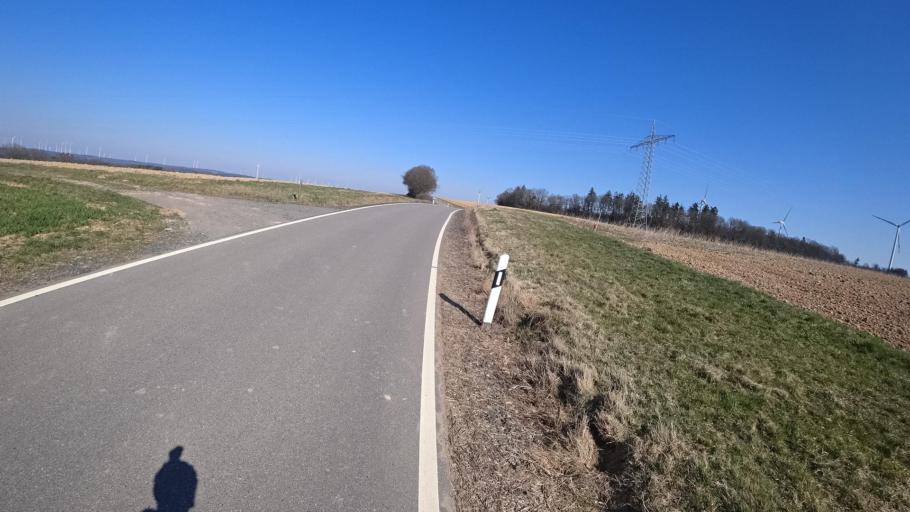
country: DE
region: Rheinland-Pfalz
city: Mutterschied
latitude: 49.9862
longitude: 7.5691
